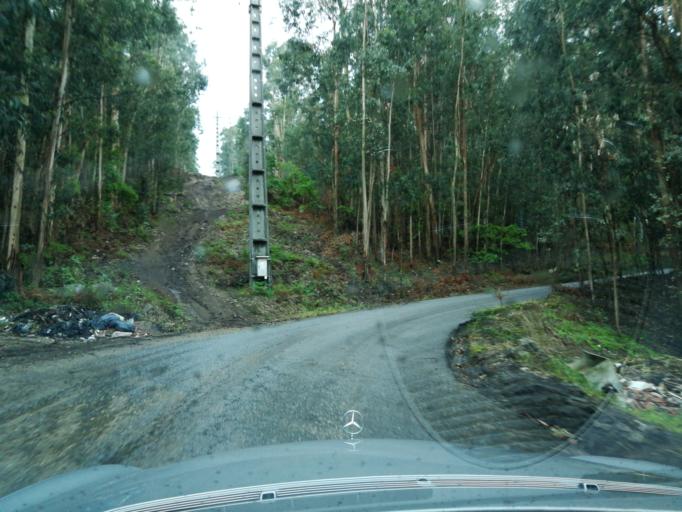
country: PT
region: Braga
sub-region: Braga
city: Oliveira
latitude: 41.4695
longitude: -8.4395
